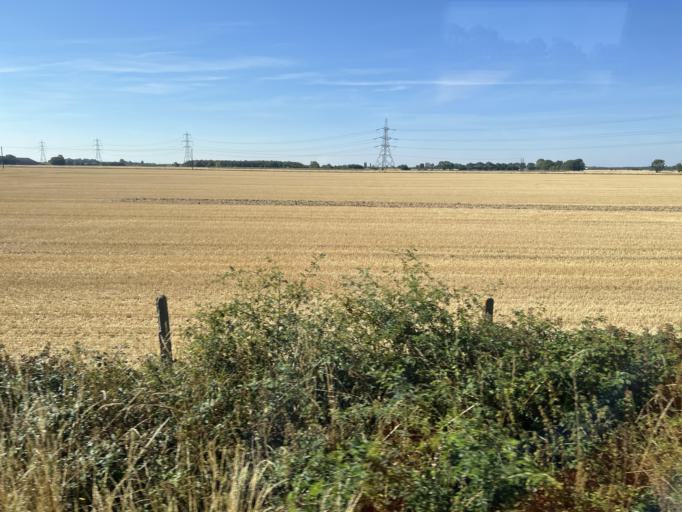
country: GB
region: England
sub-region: Lincolnshire
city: Heckington
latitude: 52.9714
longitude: -0.2620
